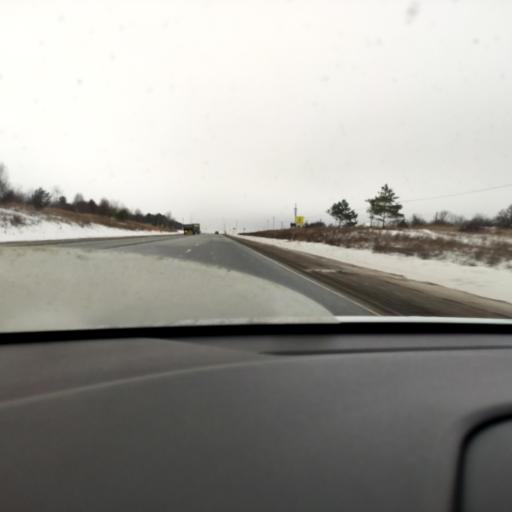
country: RU
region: Tatarstan
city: Verkhniy Uslon
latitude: 55.7224
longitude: 48.8305
